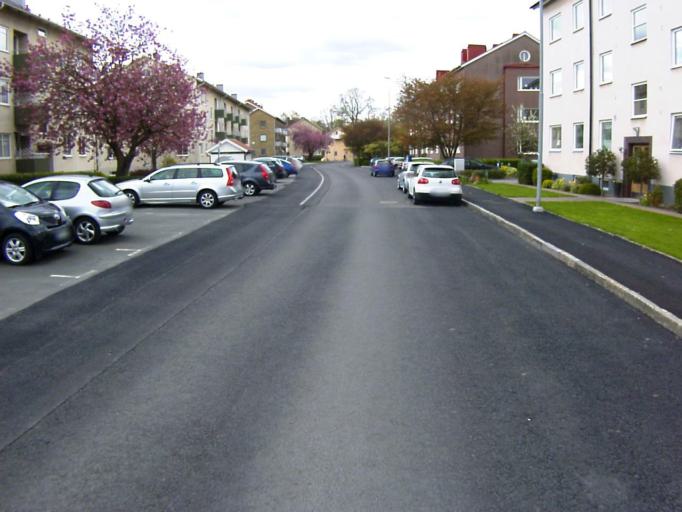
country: SE
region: Skane
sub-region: Kristianstads Kommun
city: Kristianstad
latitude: 56.0352
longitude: 14.1676
